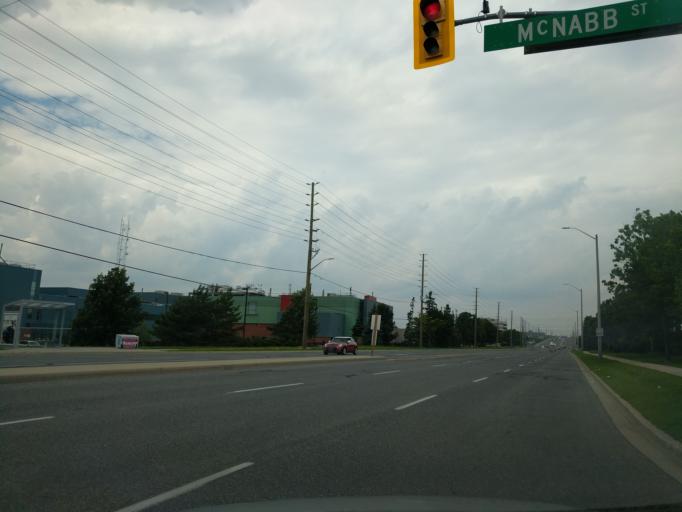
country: CA
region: Ontario
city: Markham
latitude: 43.8332
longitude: -79.3279
